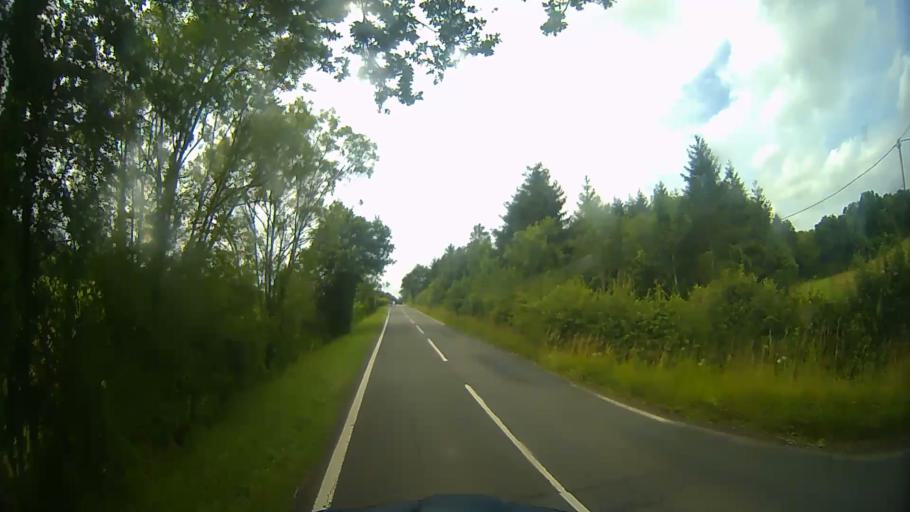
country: GB
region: England
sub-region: Hampshire
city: Kingsley
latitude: 51.1704
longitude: -0.8624
